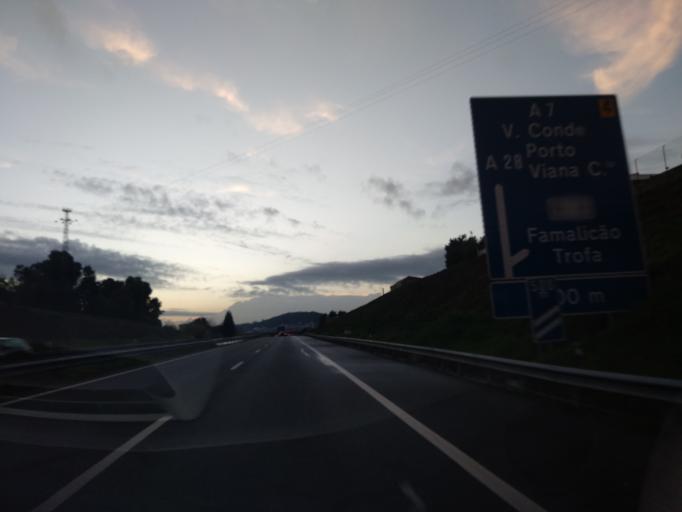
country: PT
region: Braga
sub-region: Vila Nova de Famalicao
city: Vila Nova de Famalicao
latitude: 41.3838
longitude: -8.5082
